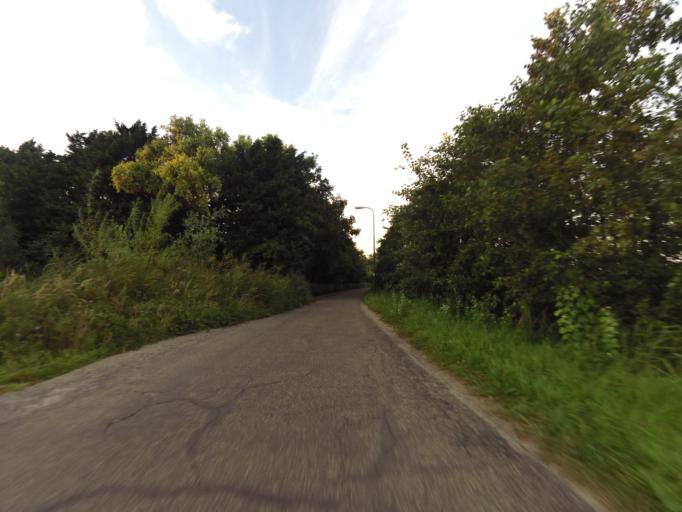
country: NL
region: South Holland
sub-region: Gemeente Katwijk
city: Rijnsburg
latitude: 52.1697
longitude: 4.4469
